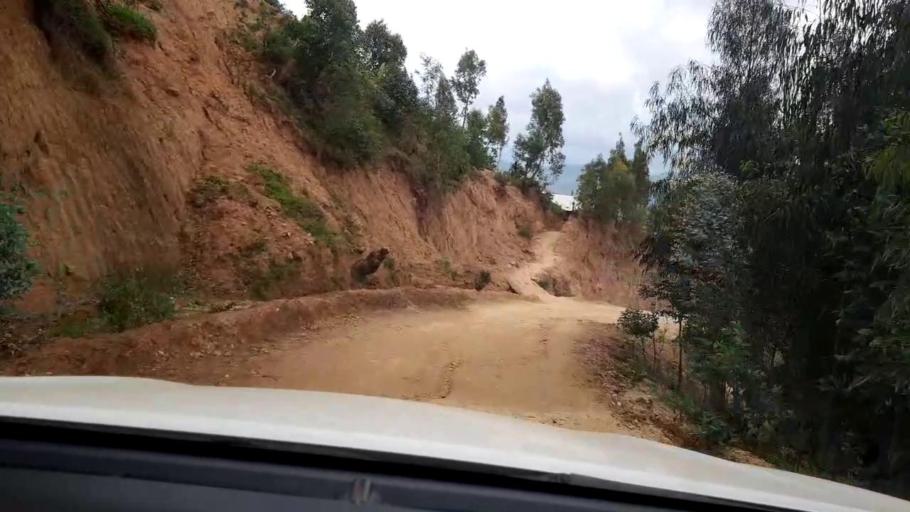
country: RW
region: Western Province
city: Kibuye
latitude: -1.8299
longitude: 29.5454
